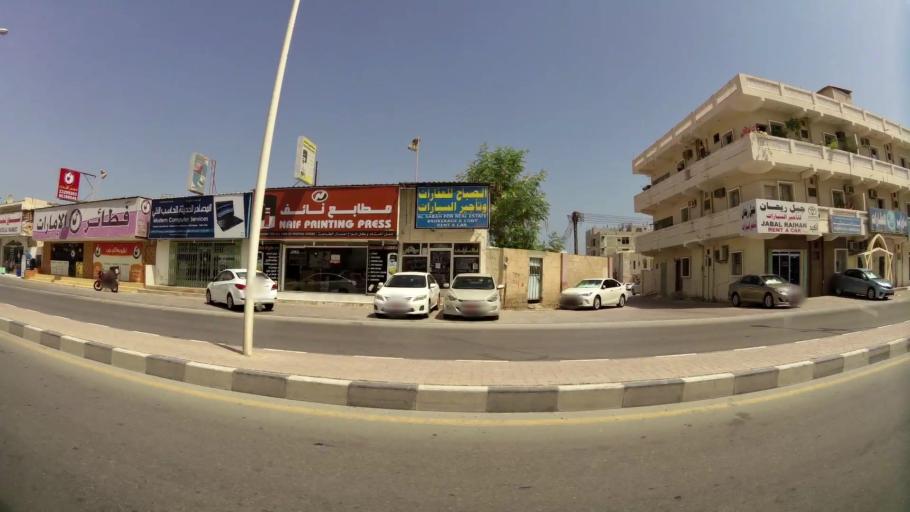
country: OM
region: Zufar
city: Salalah
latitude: 17.0137
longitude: 54.0879
